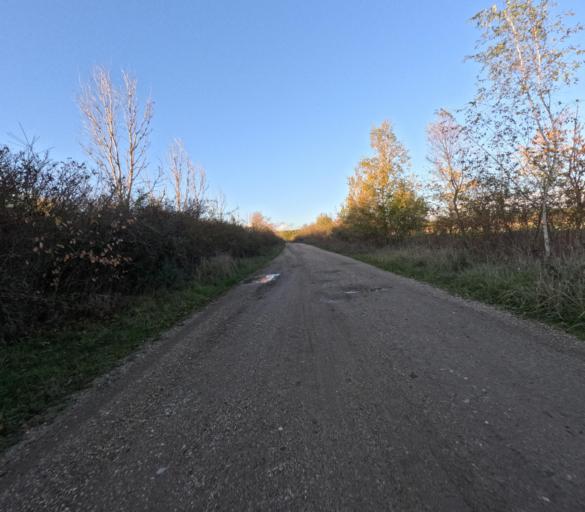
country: DE
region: Saxony-Anhalt
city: Rassnitz
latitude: 51.3818
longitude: 12.0820
